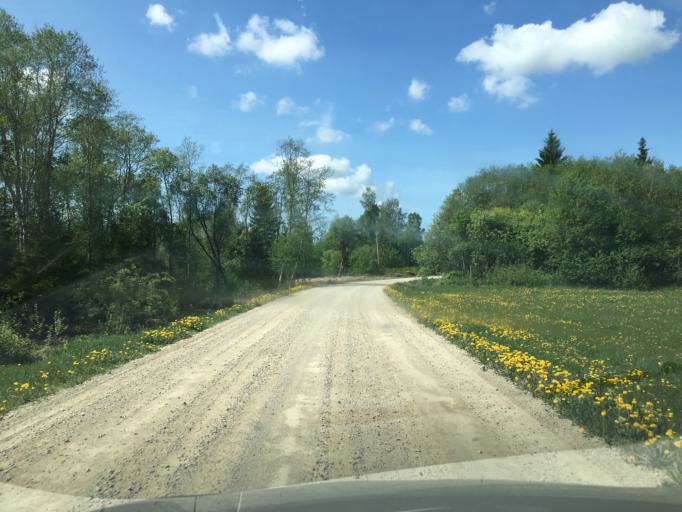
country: EE
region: Harju
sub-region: Saue linn
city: Saue
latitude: 59.2861
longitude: 24.5101
